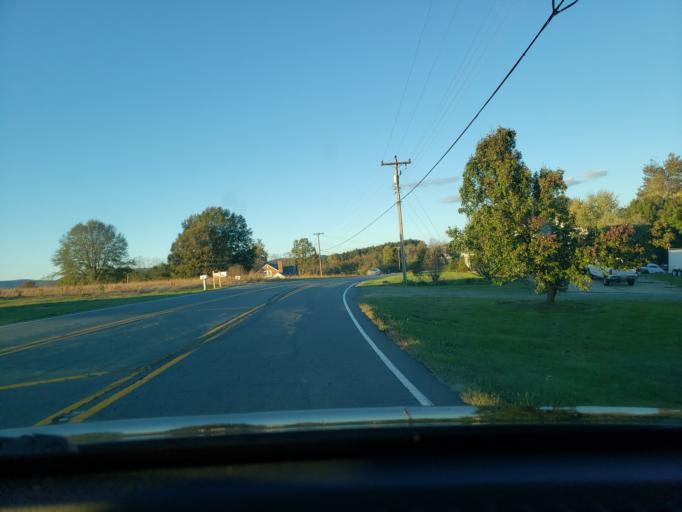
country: US
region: North Carolina
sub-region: Stokes County
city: Danbury
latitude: 36.3308
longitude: -80.2250
